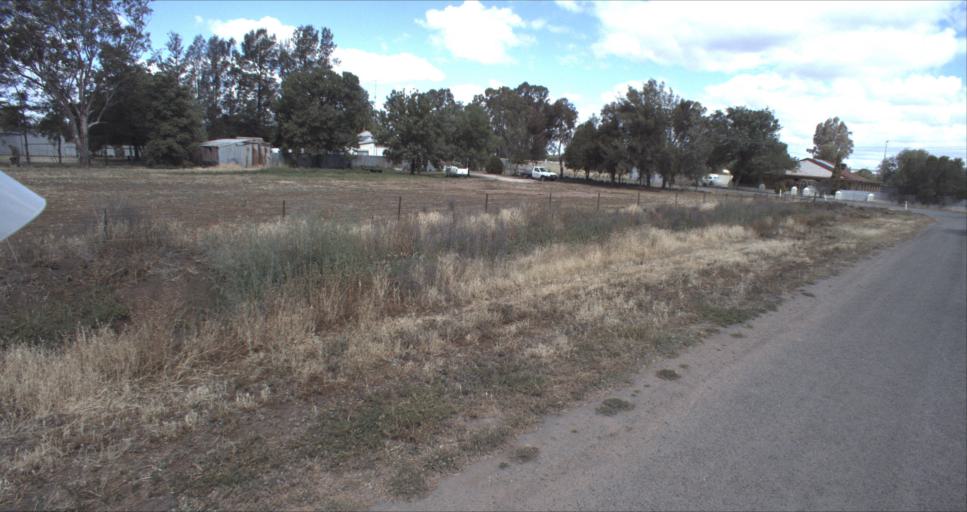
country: AU
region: New South Wales
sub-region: Leeton
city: Leeton
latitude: -34.5930
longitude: 146.4064
